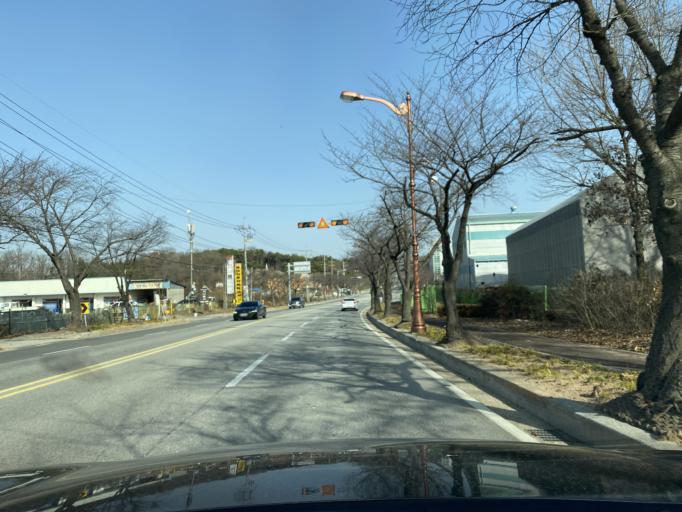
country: KR
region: Chungcheongnam-do
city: Yesan
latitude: 36.7132
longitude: 126.8415
